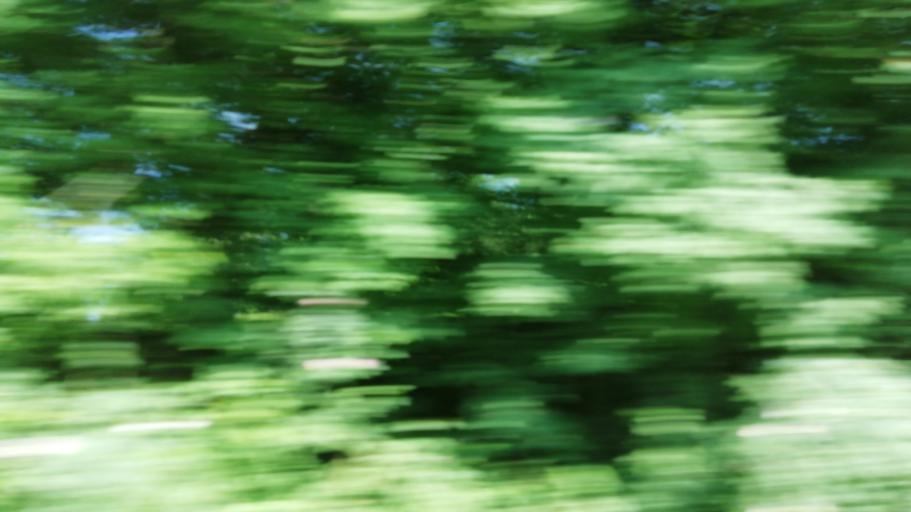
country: TR
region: Karabuk
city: Karabuk
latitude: 41.0868
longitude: 32.5828
